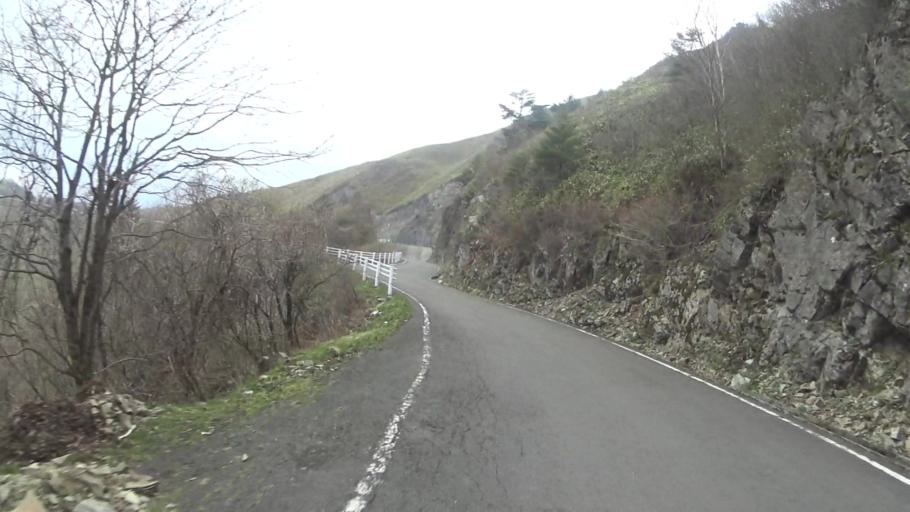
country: JP
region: Ehime
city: Saijo
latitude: 33.7827
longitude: 133.2331
